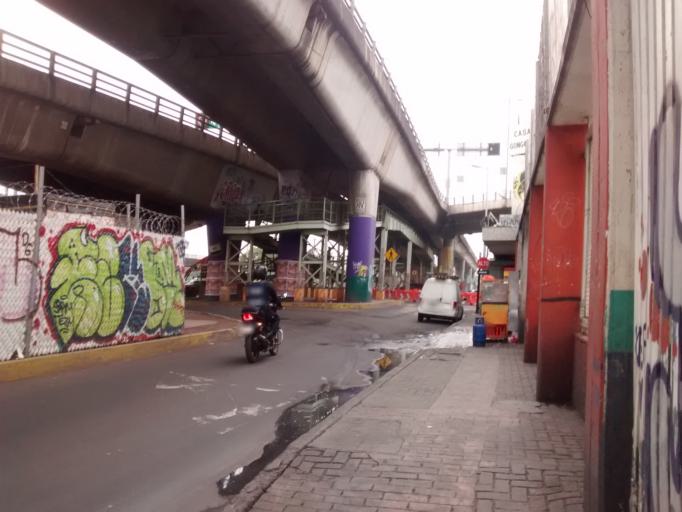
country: MX
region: Mexico City
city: Colonia Nativitas
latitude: 19.3566
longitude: -99.1107
